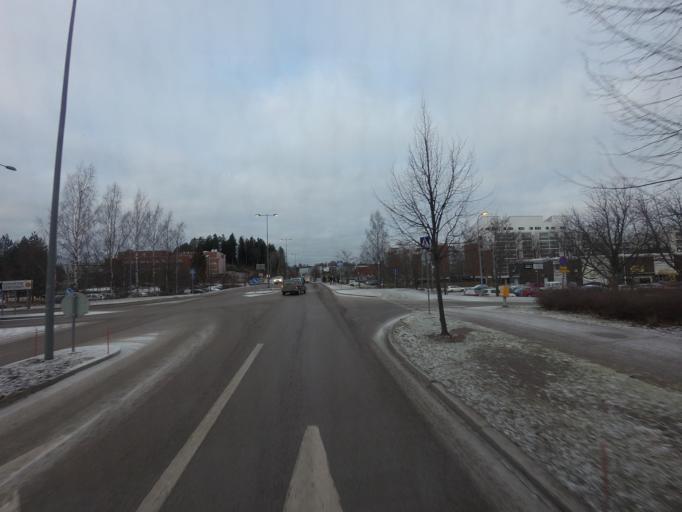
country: FI
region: Uusimaa
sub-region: Helsinki
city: Espoo
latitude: 60.2072
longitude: 24.6613
